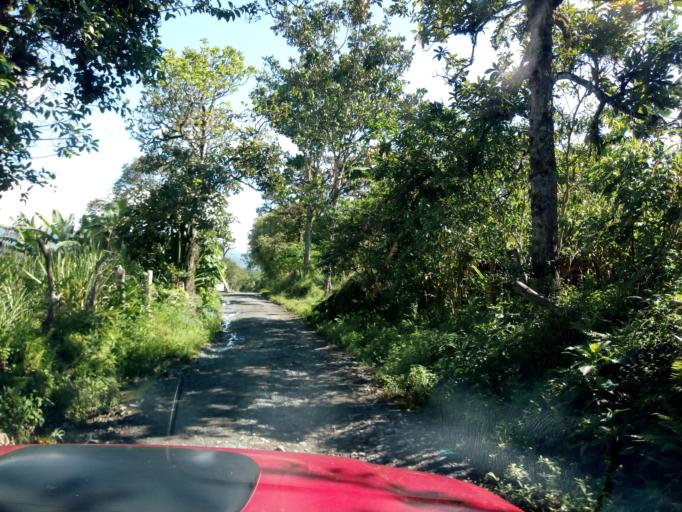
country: CO
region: Boyaca
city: Moniquira
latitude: 5.8941
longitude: -73.5329
